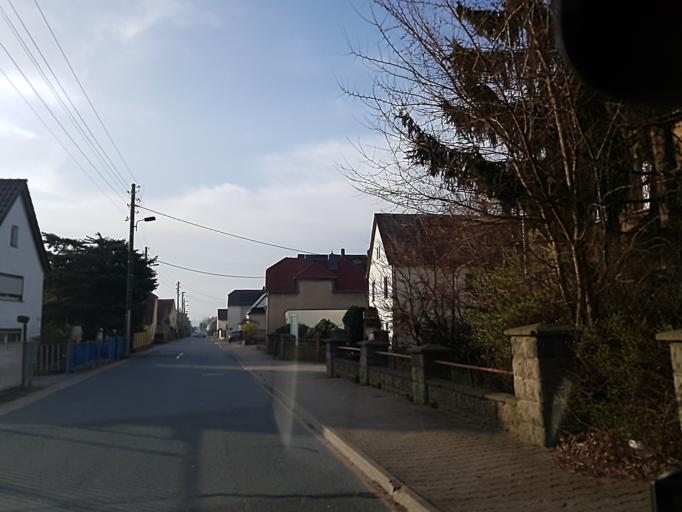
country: DE
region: Saxony
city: Riesa
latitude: 51.3234
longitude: 13.3002
